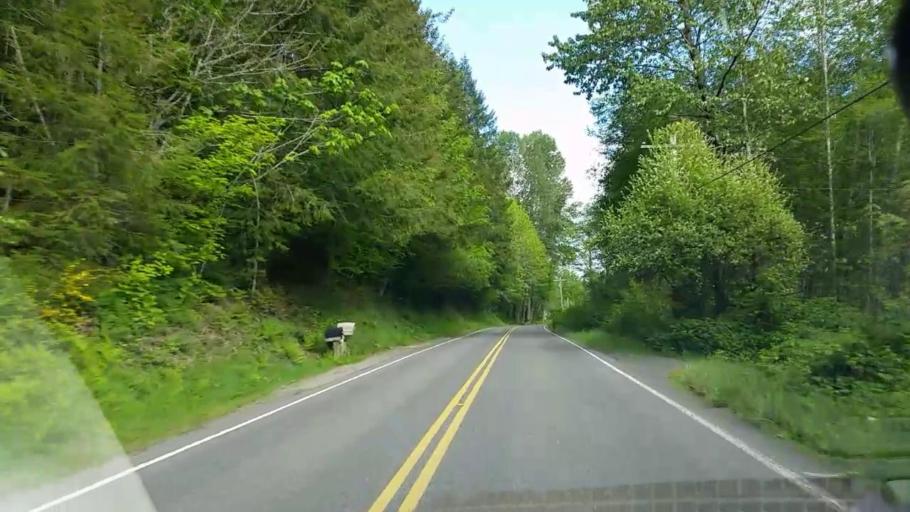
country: US
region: Washington
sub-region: Mason County
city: Shelton
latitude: 47.3202
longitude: -123.2667
